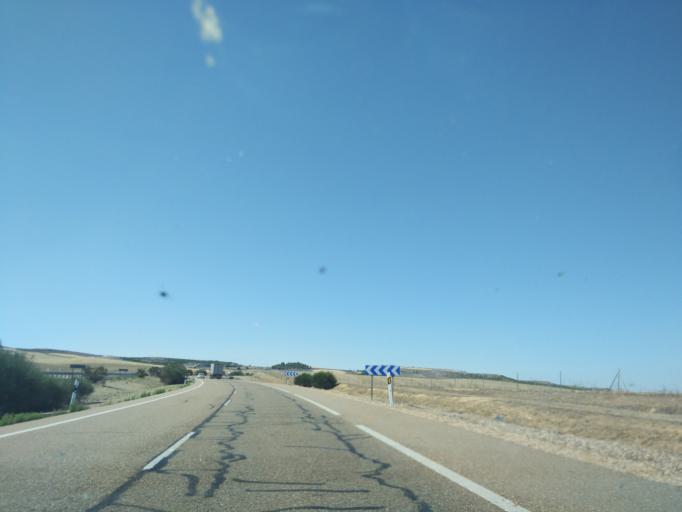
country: ES
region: Castille and Leon
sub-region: Provincia de Valladolid
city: Mota del Marques
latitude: 41.6481
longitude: -5.1898
